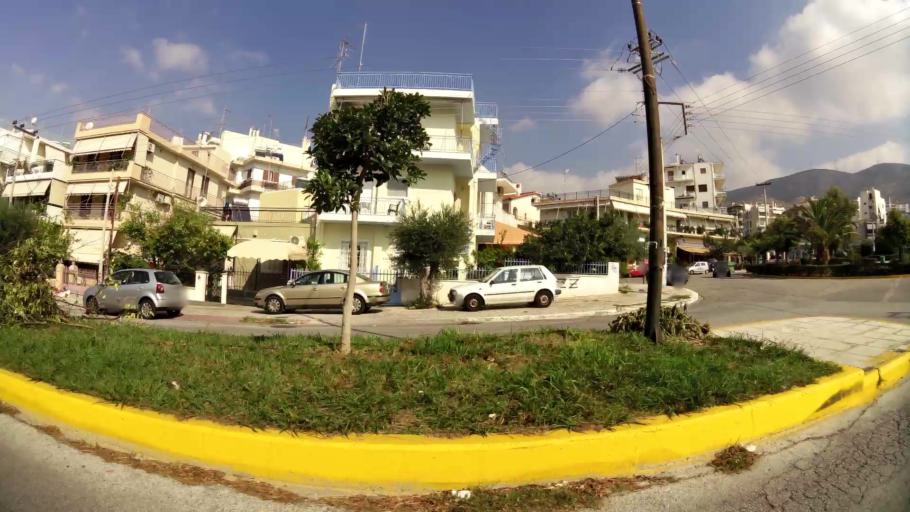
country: GR
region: Attica
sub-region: Nomarchia Athinas
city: Ilioupoli
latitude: 37.9275
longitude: 23.7546
